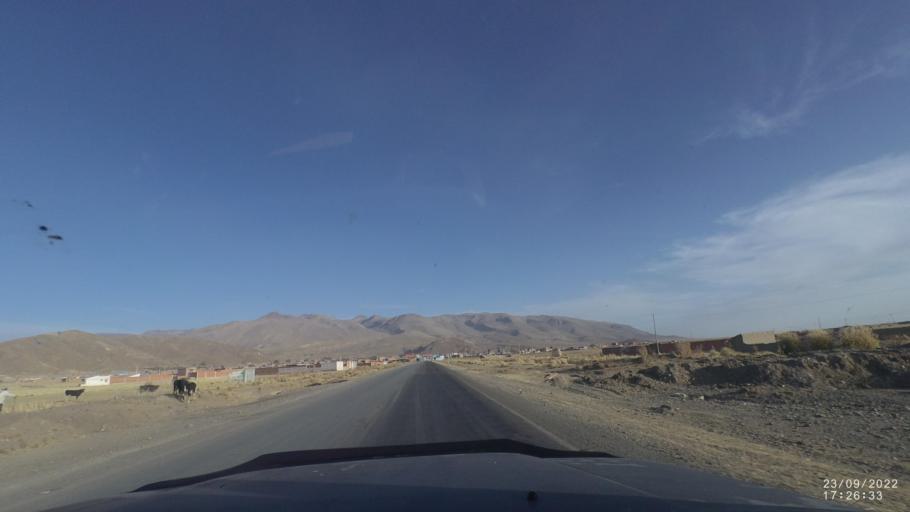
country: BO
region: Oruro
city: Challapata
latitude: -18.8864
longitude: -66.7845
